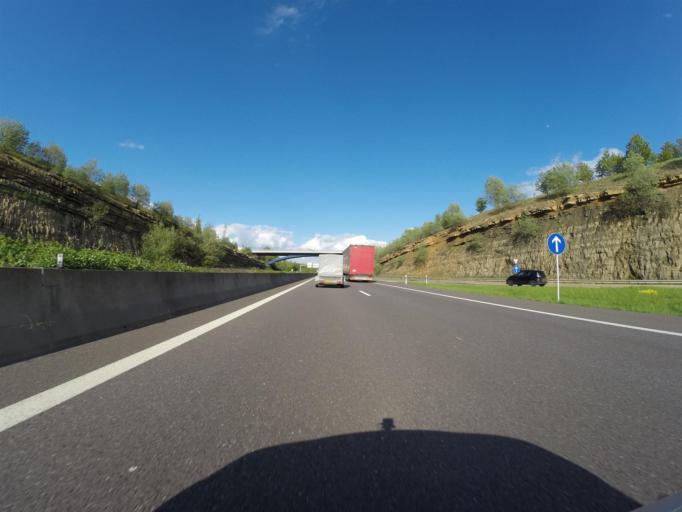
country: LU
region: Luxembourg
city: Aspelt
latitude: 49.5171
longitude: 6.2481
